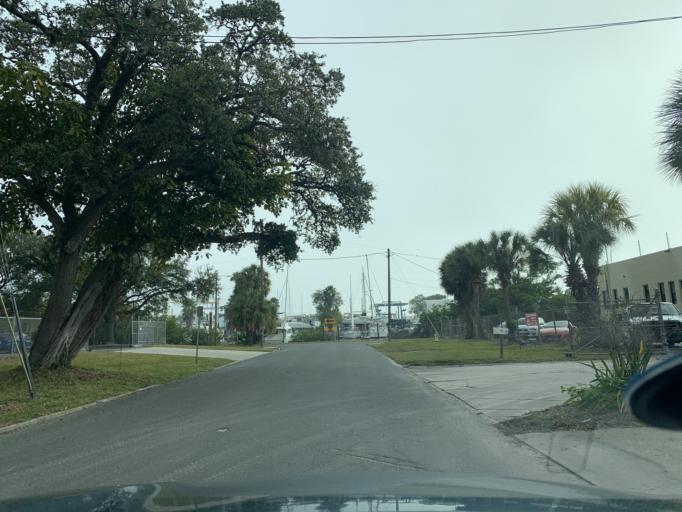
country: US
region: Florida
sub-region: Pinellas County
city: Saint Petersburg
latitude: 27.7568
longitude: -82.6345
